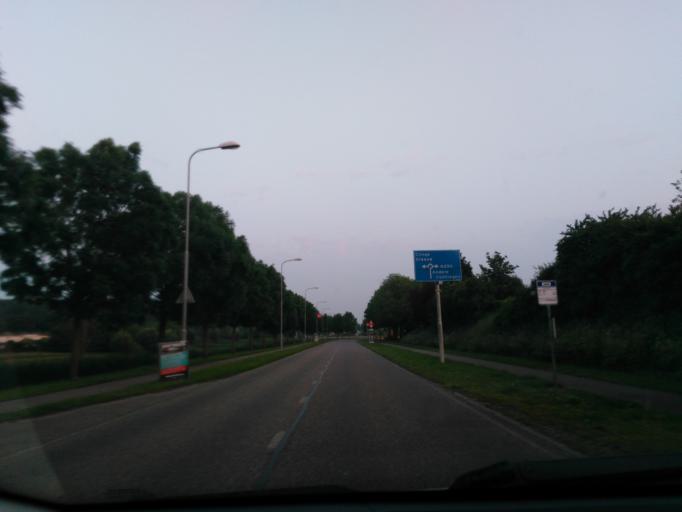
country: NL
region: Zeeland
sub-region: Gemeente Hulst
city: Hulst
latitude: 51.2739
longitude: 4.0535
